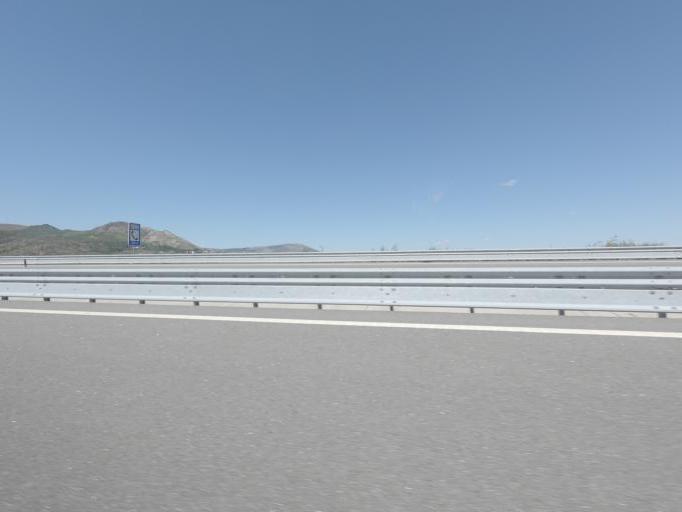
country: PT
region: Vila Real
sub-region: Santa Marta de Penaguiao
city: Santa Marta de Penaguiao
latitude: 41.2757
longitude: -7.8196
